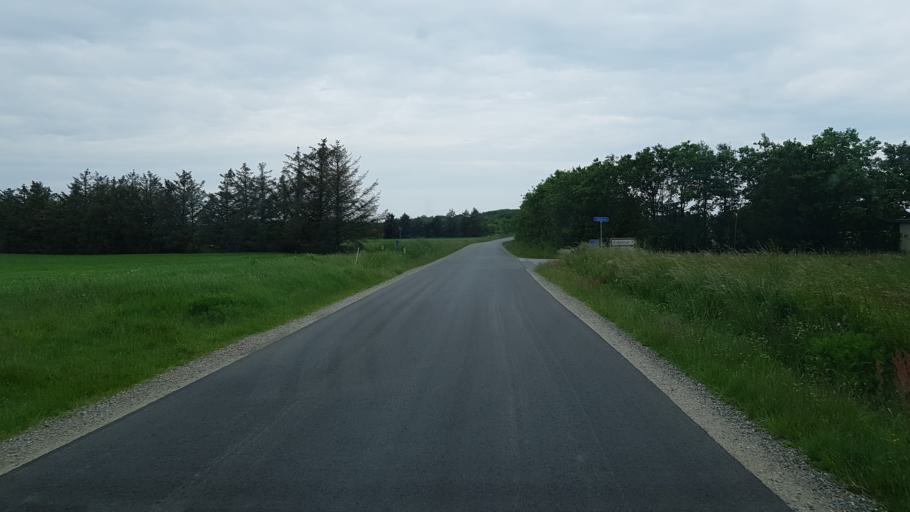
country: DK
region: South Denmark
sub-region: Varde Kommune
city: Oksbol
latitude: 55.7469
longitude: 8.3724
